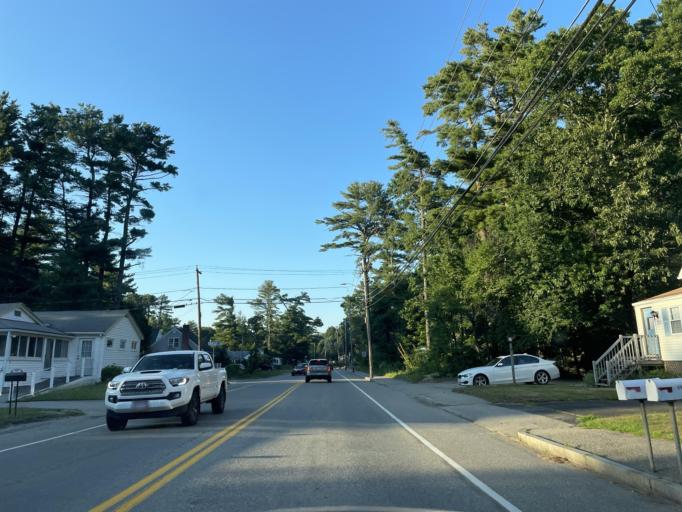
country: US
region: Massachusetts
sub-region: Plymouth County
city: Halifax
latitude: 42.0187
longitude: -70.8426
